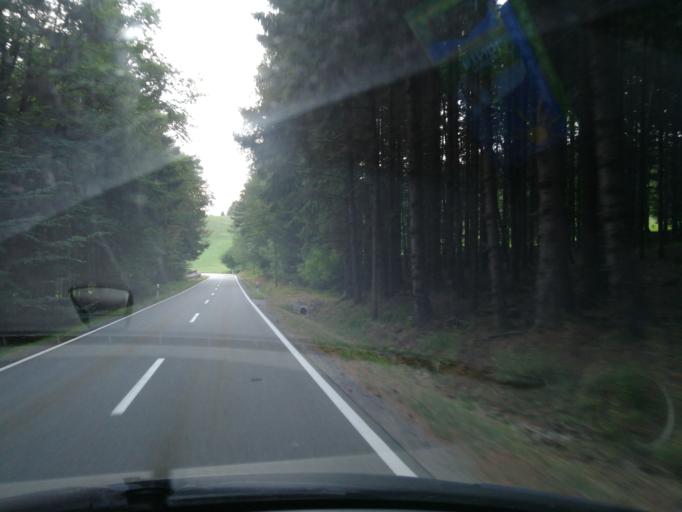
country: DE
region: Bavaria
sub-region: Lower Bavaria
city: Haibach
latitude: 49.0372
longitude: 12.7545
